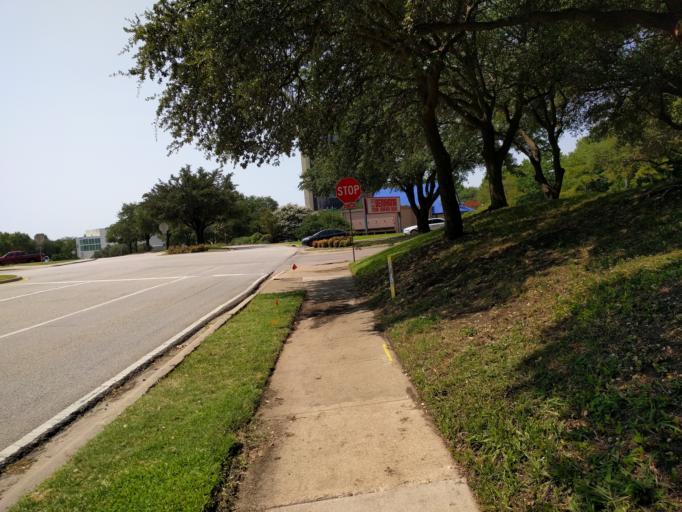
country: US
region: Texas
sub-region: Dallas County
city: Richardson
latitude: 32.9215
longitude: -96.7718
